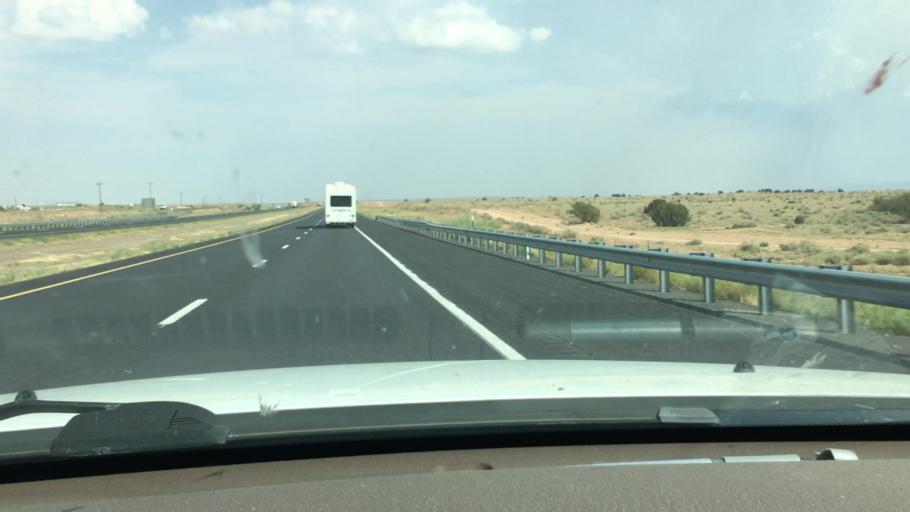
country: US
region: New Mexico
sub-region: Cibola County
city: Laguna
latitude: 35.0027
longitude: -107.3111
